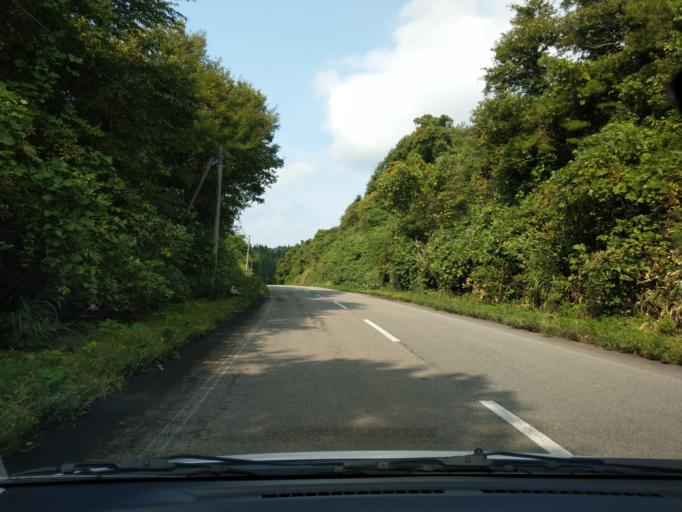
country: JP
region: Akita
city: Omagari
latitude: 39.4937
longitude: 140.3125
